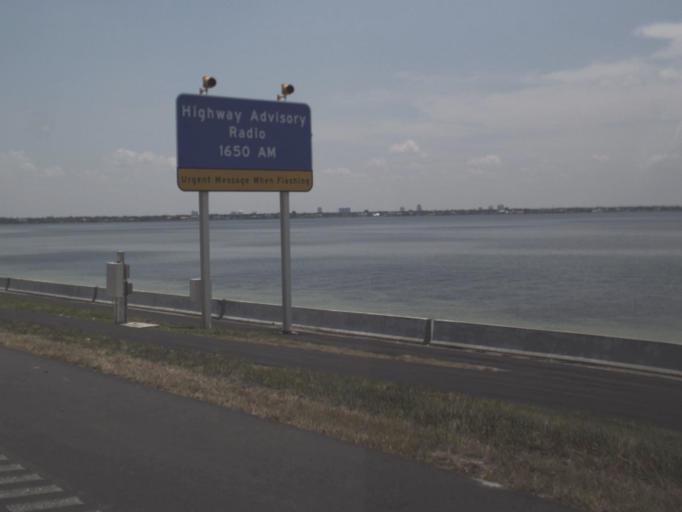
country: US
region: Florida
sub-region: Hillsborough County
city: Town 'n' Country
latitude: 27.9364
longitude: -82.5628
